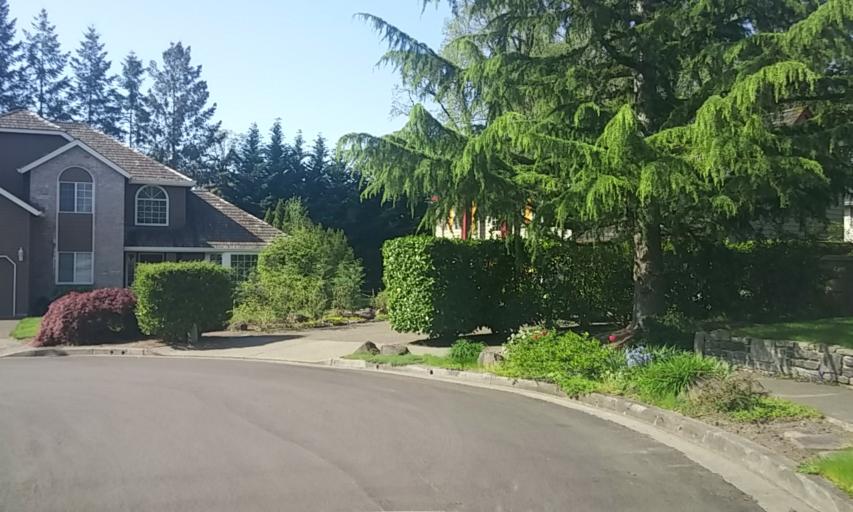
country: US
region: Oregon
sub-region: Washington County
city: Metzger
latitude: 45.4309
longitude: -122.7371
